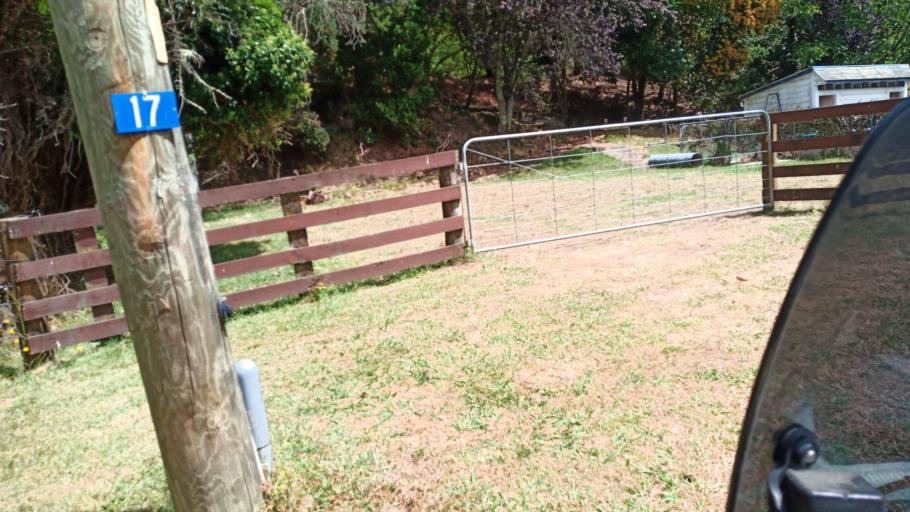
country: NZ
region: Gisborne
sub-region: Gisborne District
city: Gisborne
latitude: -38.4630
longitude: 177.6533
